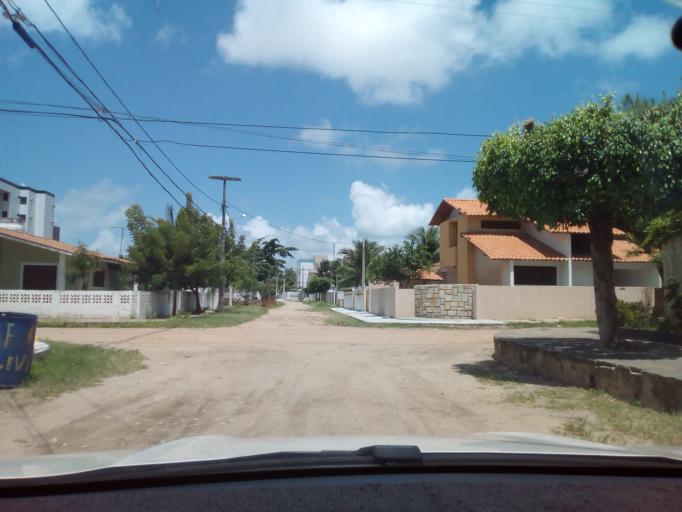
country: BR
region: Paraiba
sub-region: Cabedelo
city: Cabedelo
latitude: -7.0120
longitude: -34.8306
